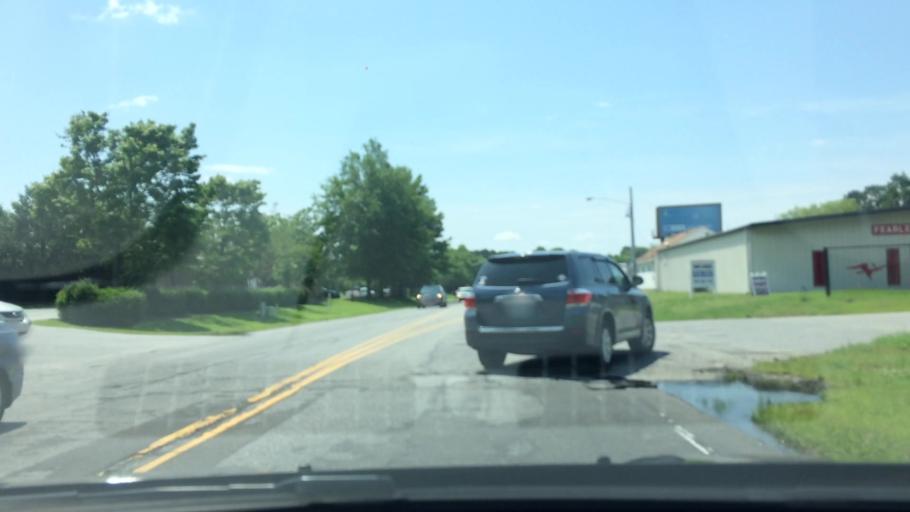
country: US
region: North Carolina
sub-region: Pitt County
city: Windsor
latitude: 35.5628
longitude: -77.3554
